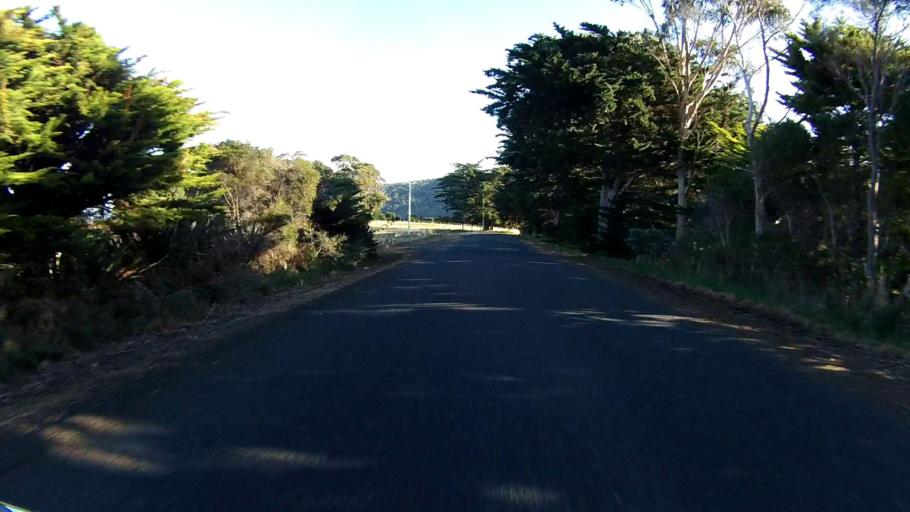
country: AU
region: Tasmania
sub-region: Clarence
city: Sandford
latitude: -43.1704
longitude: 147.8563
